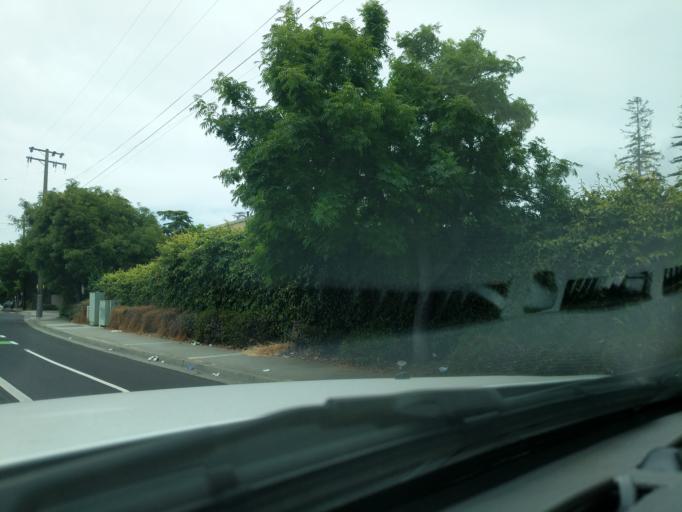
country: US
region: California
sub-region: Alameda County
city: Hayward
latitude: 37.6458
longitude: -122.0670
